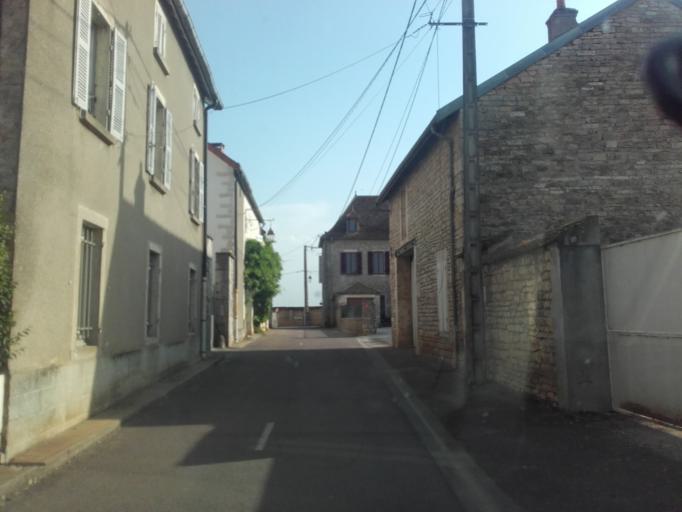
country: FR
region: Bourgogne
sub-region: Departement de la Cote-d'Or
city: Meursault
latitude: 46.9744
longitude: 4.7675
